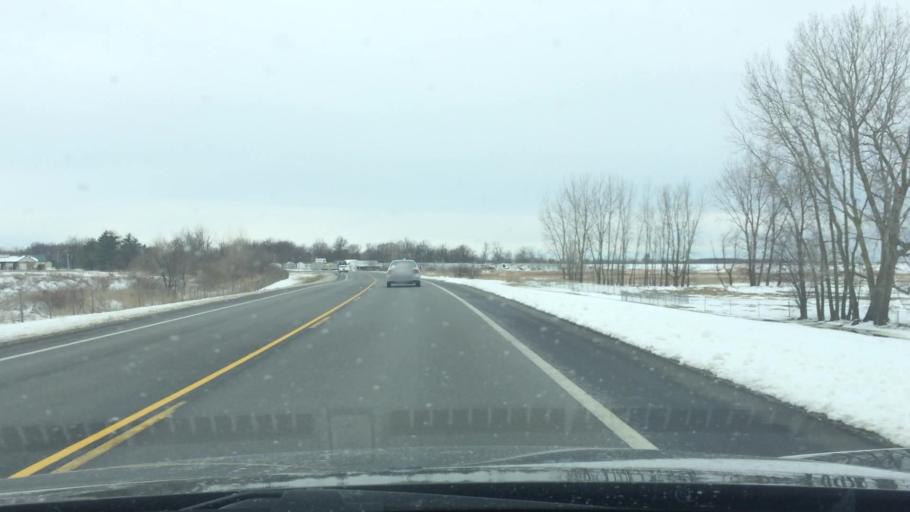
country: US
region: Ohio
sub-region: Logan County
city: Russells Point
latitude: 40.4776
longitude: -83.9018
